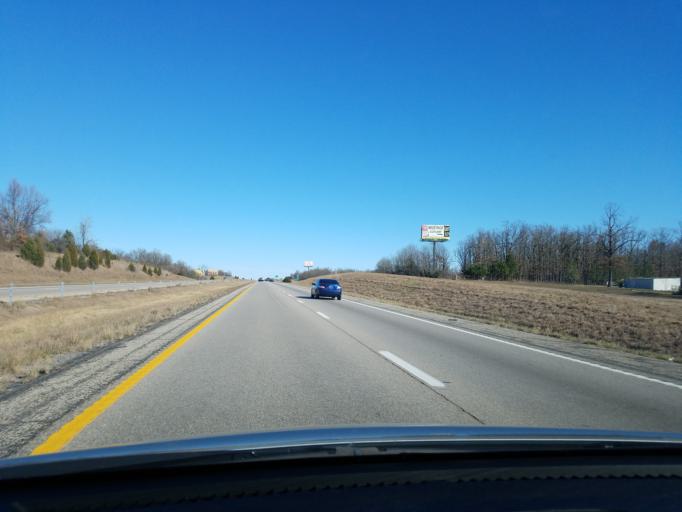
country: US
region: Missouri
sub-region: Laclede County
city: Lebanon
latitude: 37.5867
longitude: -92.7390
